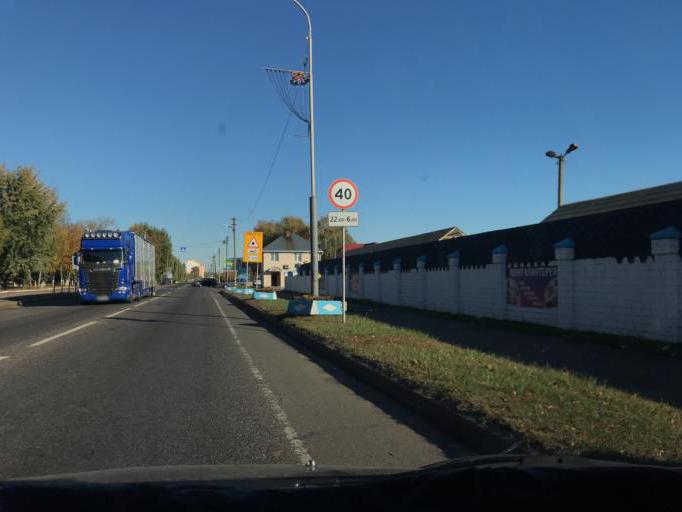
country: BY
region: Gomel
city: Kalinkavichy
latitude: 52.1256
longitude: 29.3359
